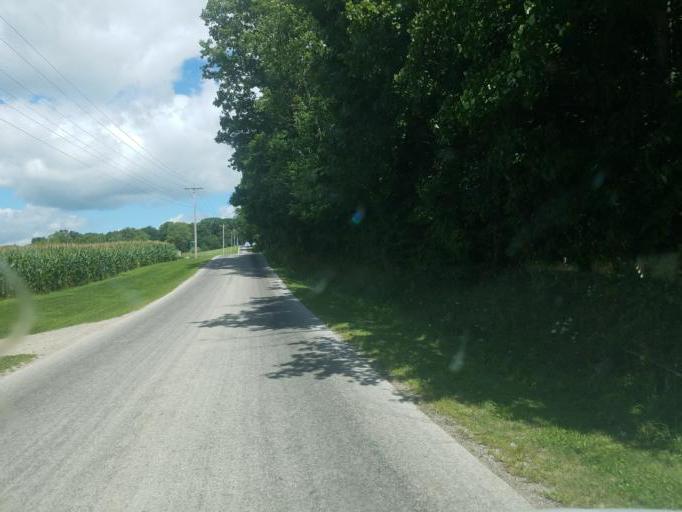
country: US
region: Ohio
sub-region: Knox County
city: Fredericktown
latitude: 40.5592
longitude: -82.6047
